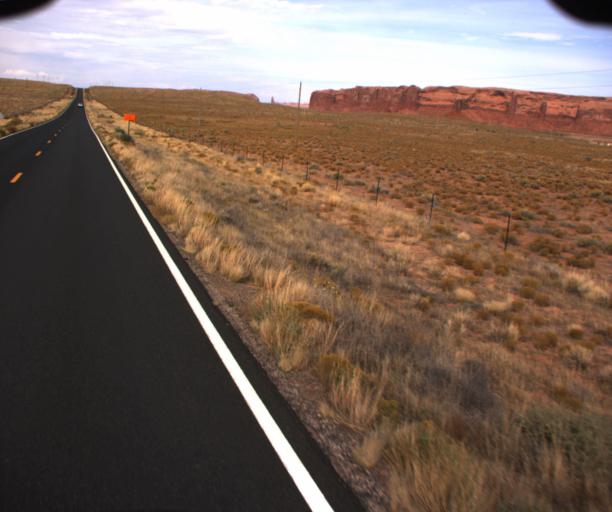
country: US
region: Arizona
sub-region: Apache County
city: Many Farms
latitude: 36.5911
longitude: -109.5624
